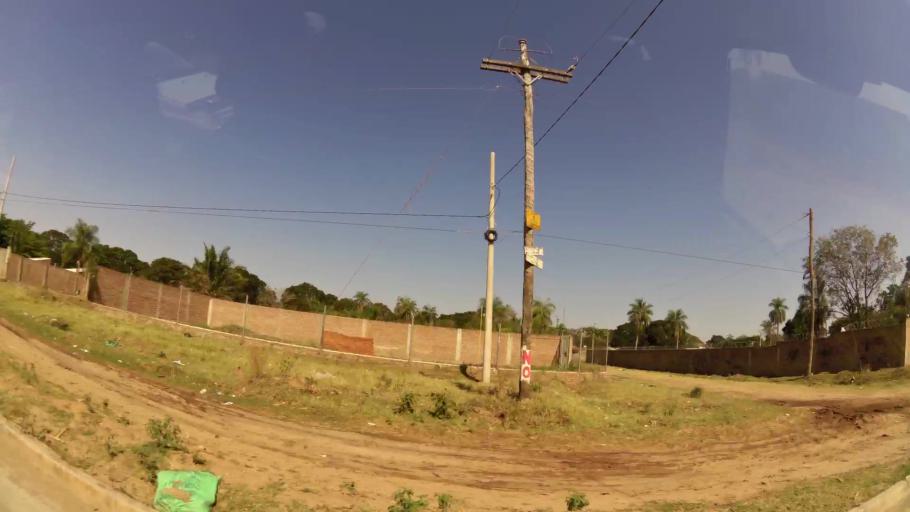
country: BO
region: Santa Cruz
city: Cotoca
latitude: -17.7240
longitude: -63.0818
